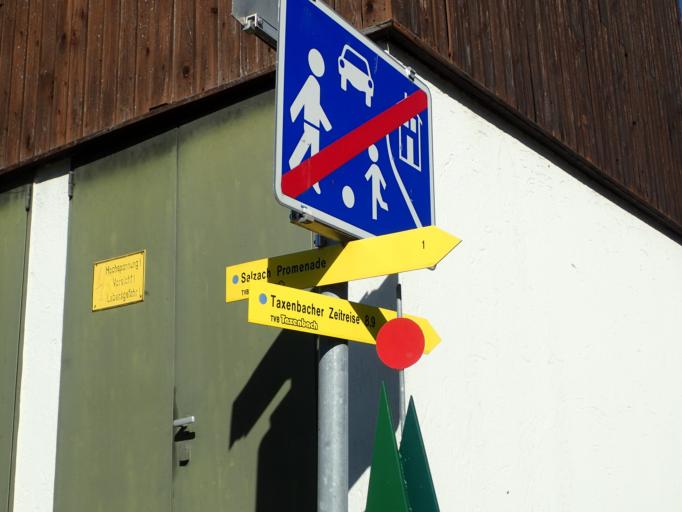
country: AT
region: Salzburg
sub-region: Politischer Bezirk Zell am See
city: Taxenbach
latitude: 47.2914
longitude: 12.9614
